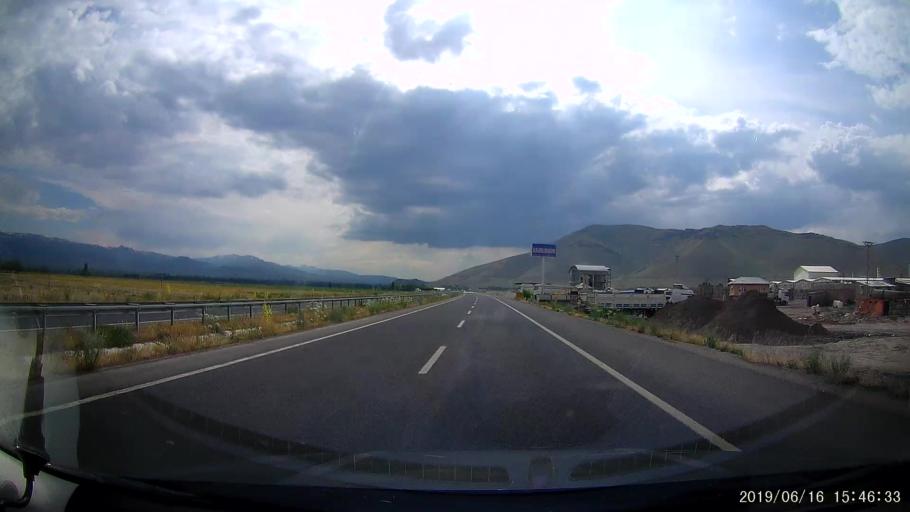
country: TR
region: Erzurum
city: Pasinler
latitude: 39.9899
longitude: 41.7414
